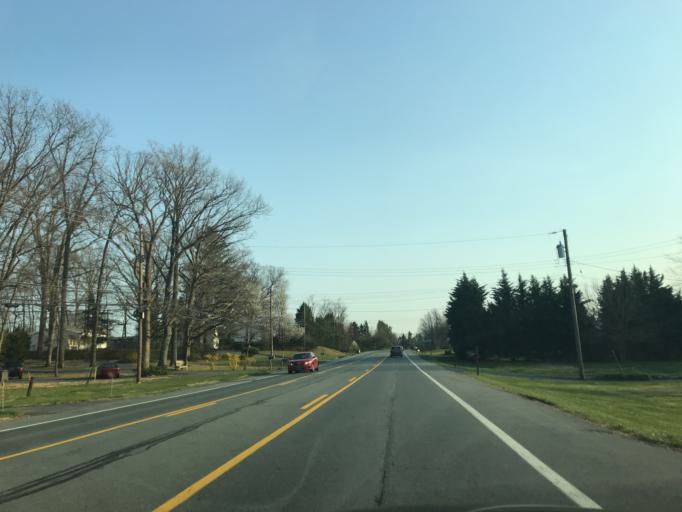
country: US
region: Maryland
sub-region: Howard County
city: Ellicott City
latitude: 39.2337
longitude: -76.7985
